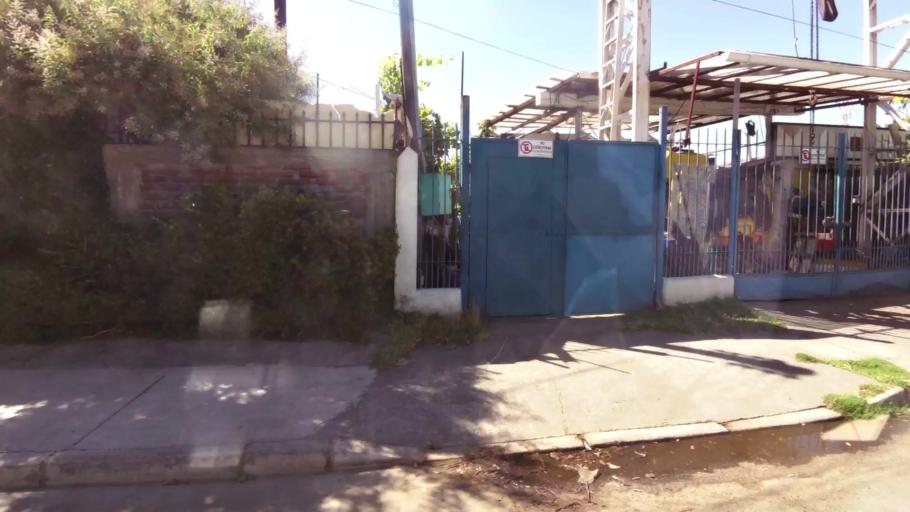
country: CL
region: O'Higgins
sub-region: Provincia de Cachapoal
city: Rancagua
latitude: -34.1789
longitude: -70.7360
